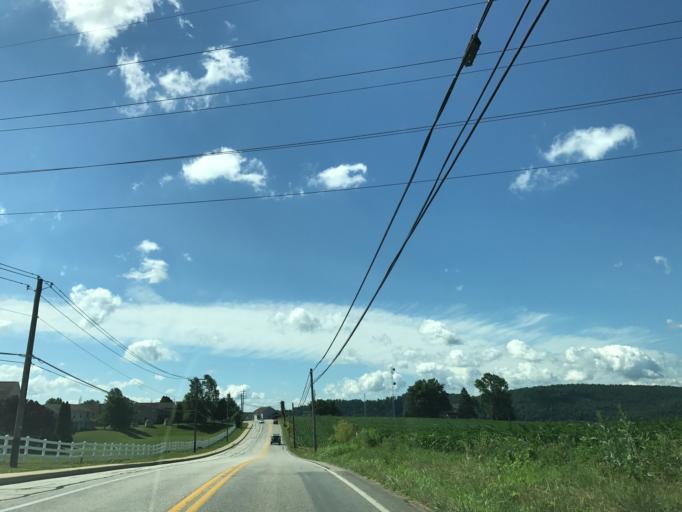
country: US
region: Pennsylvania
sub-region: Lancaster County
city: Maytown
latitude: 40.0687
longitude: -76.5768
